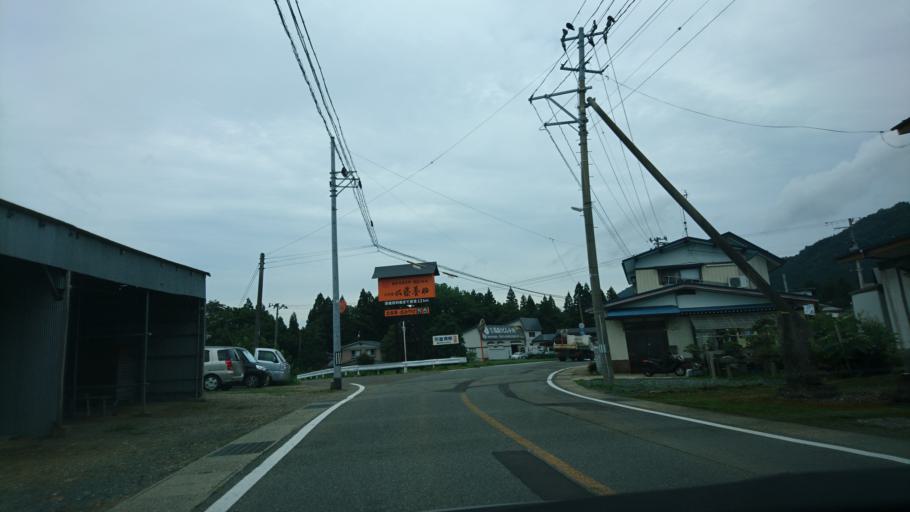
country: JP
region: Akita
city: Yuzawa
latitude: 39.1094
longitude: 140.5825
